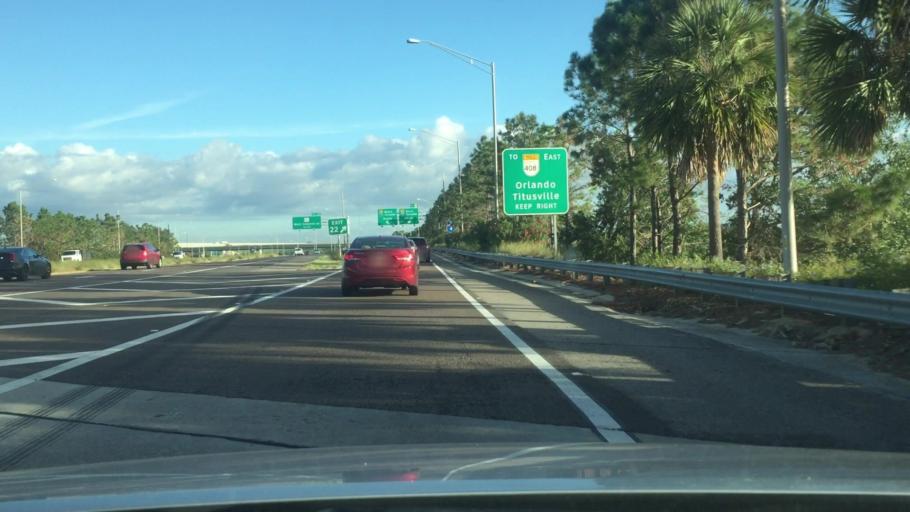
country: US
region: Florida
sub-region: Orange County
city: Ocoee
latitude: 28.5383
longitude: -81.5568
